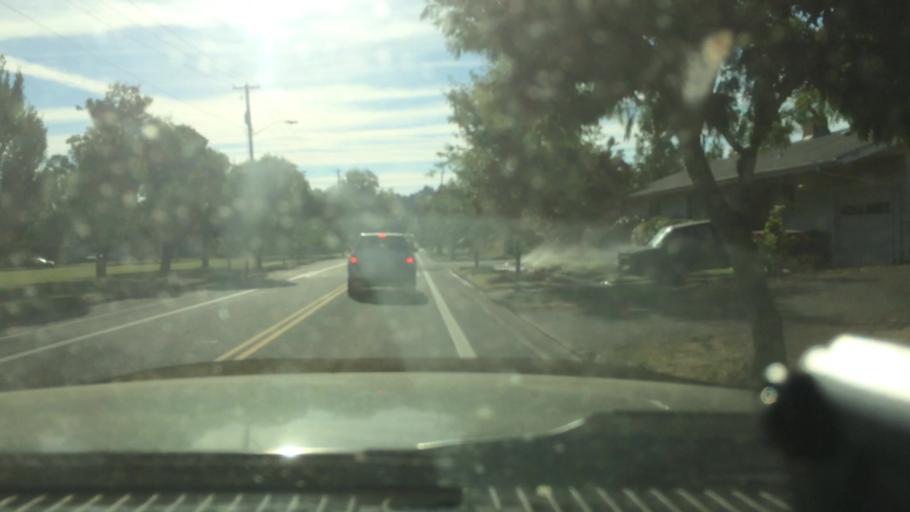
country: US
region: Oregon
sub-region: Lane County
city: Eugene
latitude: 44.0331
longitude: -123.1138
